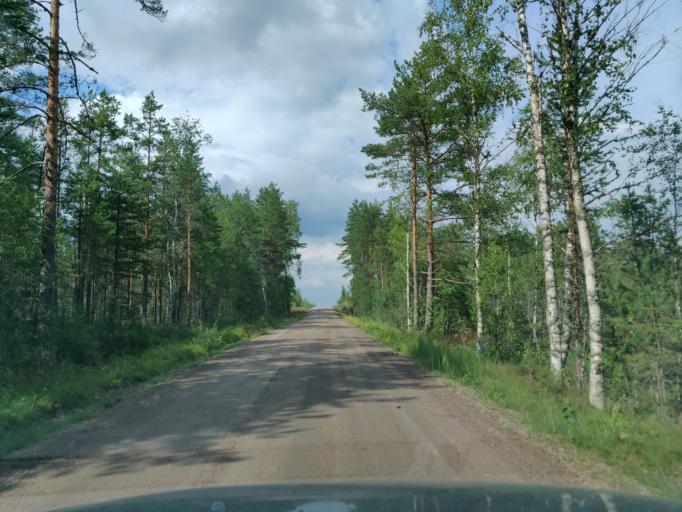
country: SE
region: Vaermland
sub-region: Hagfors Kommun
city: Hagfors
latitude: 59.9738
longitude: 13.5484
